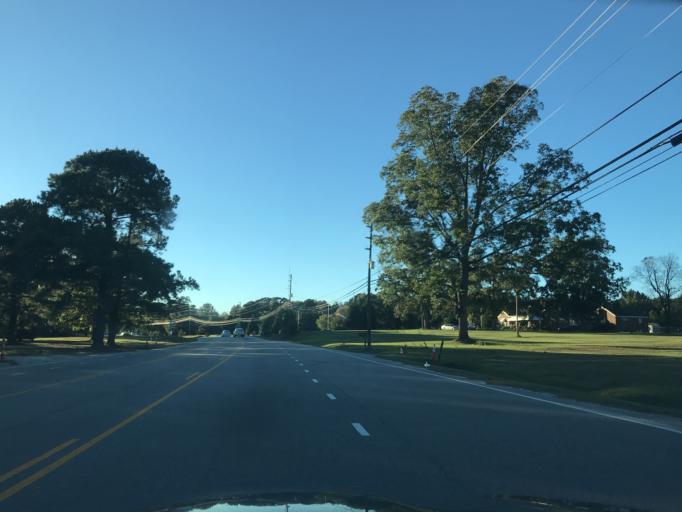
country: US
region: North Carolina
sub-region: Wake County
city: Garner
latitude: 35.7471
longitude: -78.5880
